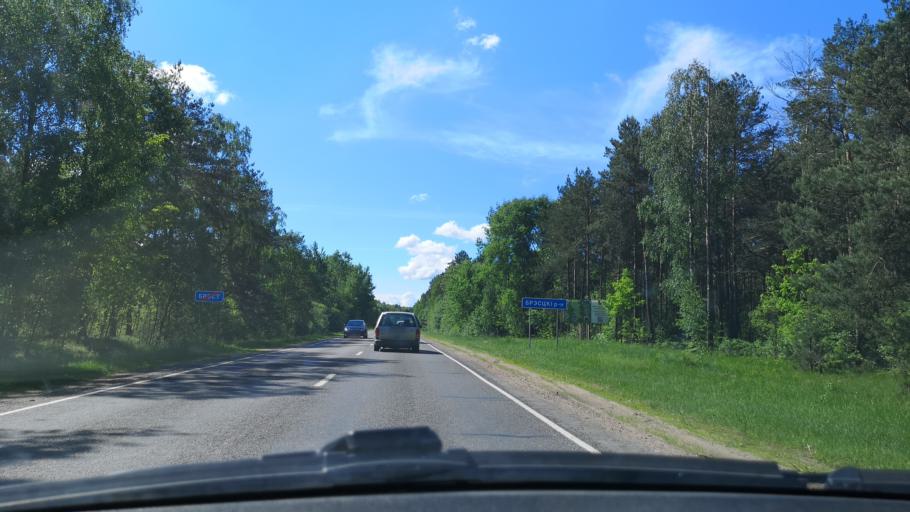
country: BY
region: Brest
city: Brest
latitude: 52.0277
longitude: 23.7296
